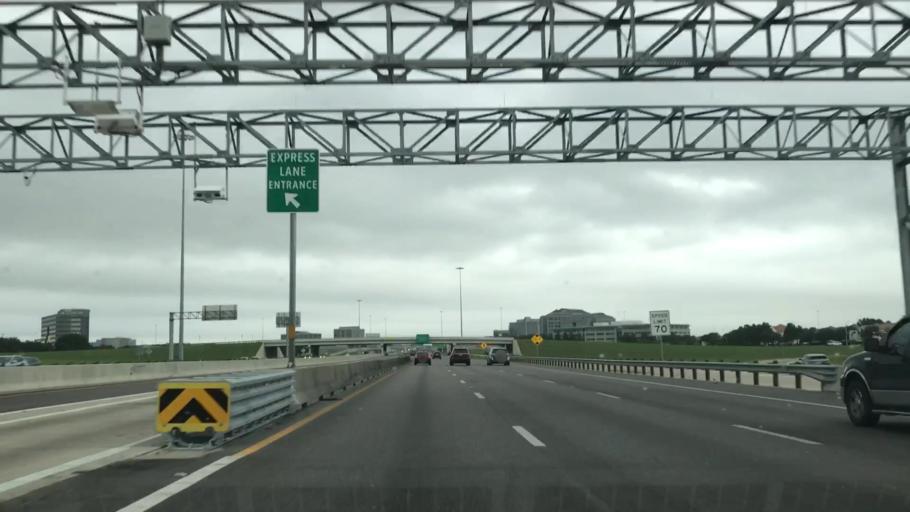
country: US
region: Texas
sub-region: Dallas County
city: Farmers Branch
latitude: 32.8887
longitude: -96.9592
